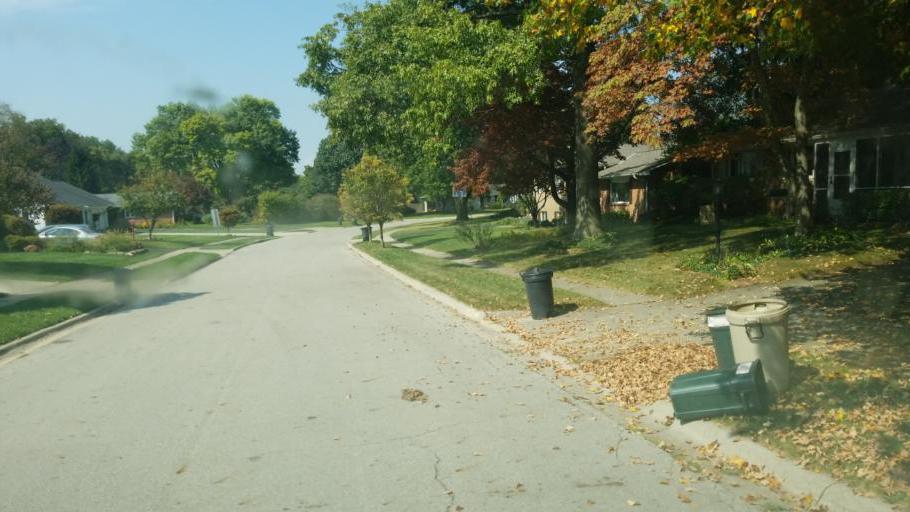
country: US
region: Ohio
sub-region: Franklin County
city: Worthington
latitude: 40.0862
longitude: -83.0254
